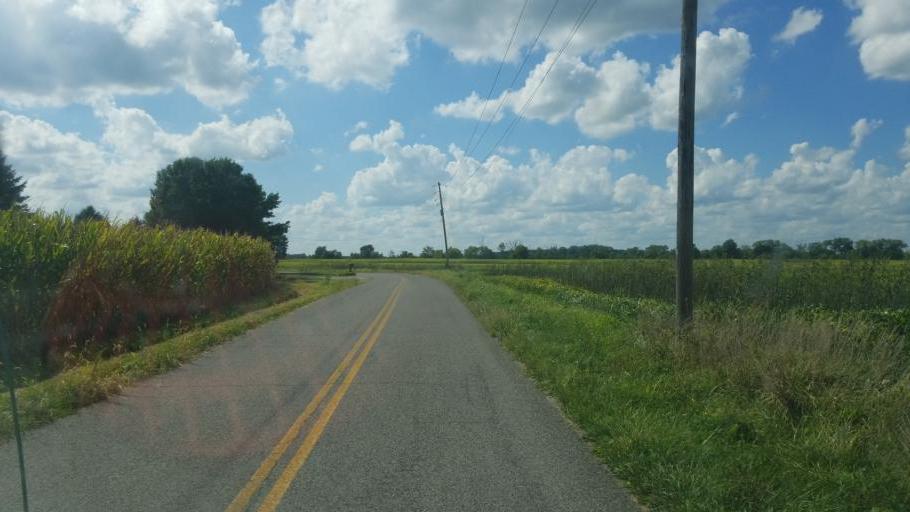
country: US
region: Ohio
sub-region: Union County
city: Richwood
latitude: 40.4346
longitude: -83.3266
